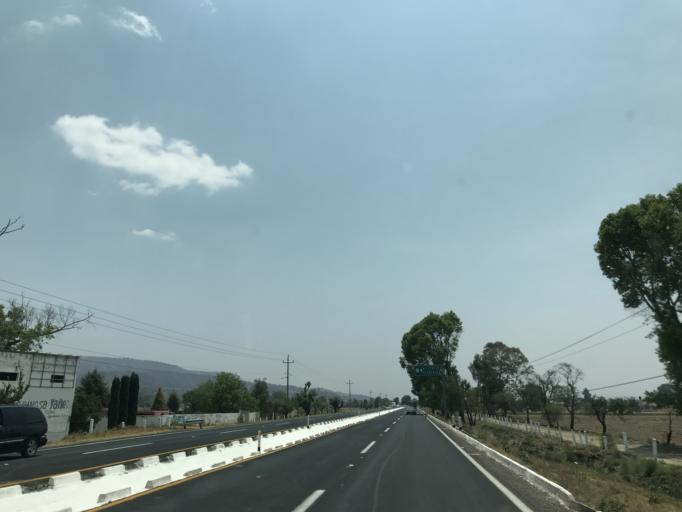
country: MX
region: Tlaxcala
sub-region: Ixtacuixtla de Mariano Matamoros
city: Santa Justina Ecatepec
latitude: 19.3266
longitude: -98.3258
